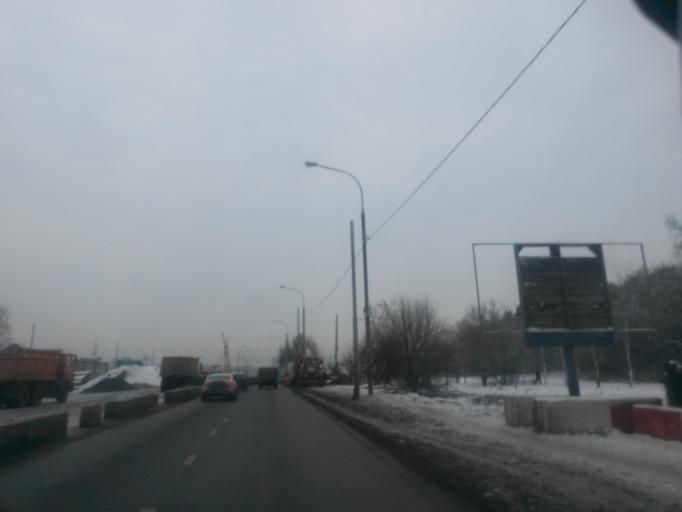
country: RU
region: Moscow
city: Mikhalkovo
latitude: 55.6929
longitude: 37.4255
